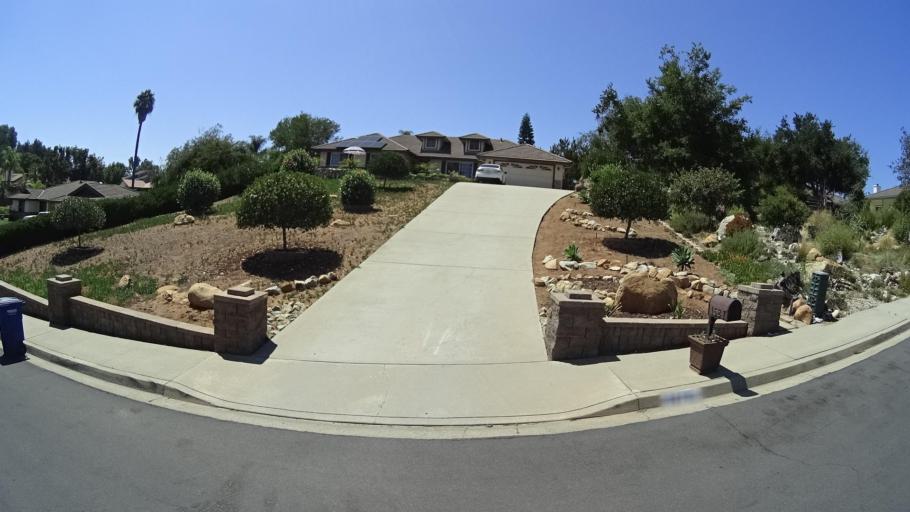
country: US
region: California
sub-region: San Diego County
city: Fallbrook
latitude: 33.3645
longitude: -117.2551
